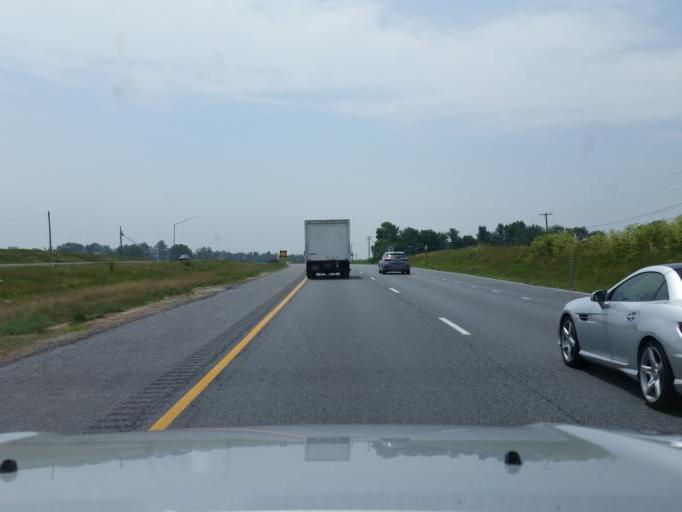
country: US
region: Maryland
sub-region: Frederick County
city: Clover Hill
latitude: 39.4884
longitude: -77.3980
